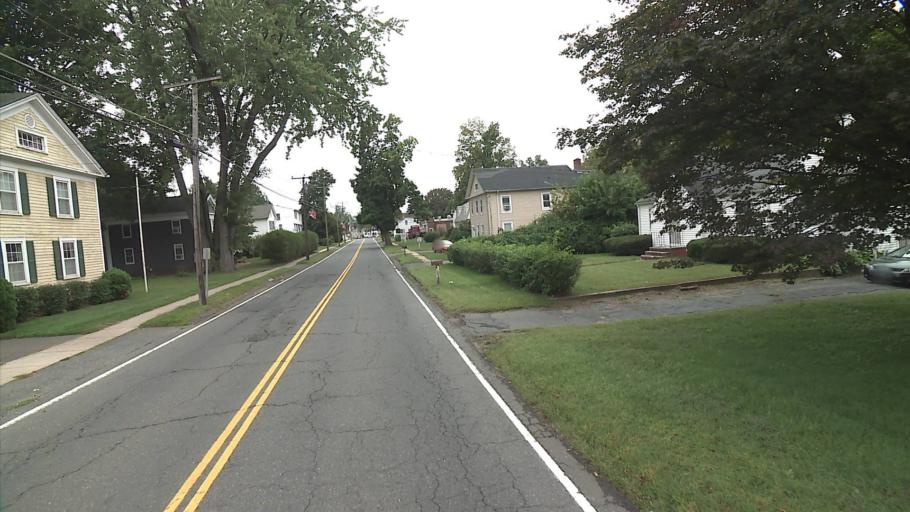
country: US
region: Connecticut
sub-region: Hartford County
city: Windsor Locks
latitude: 41.9319
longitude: -72.6180
